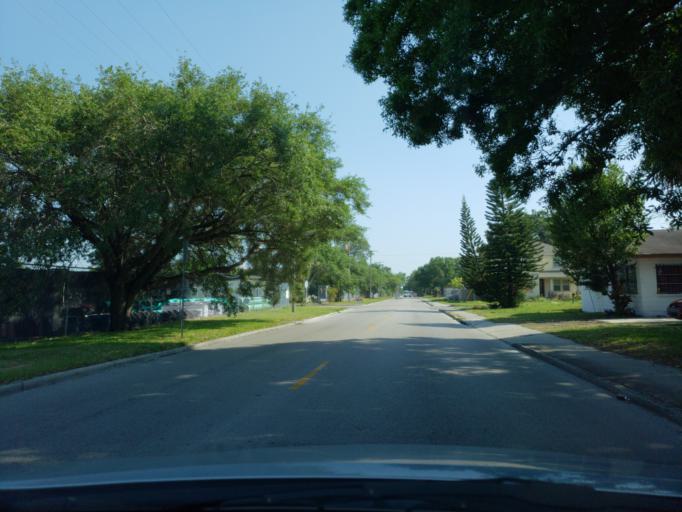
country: US
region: Florida
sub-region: Hillsborough County
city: Tampa
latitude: 27.9635
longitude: -82.4766
